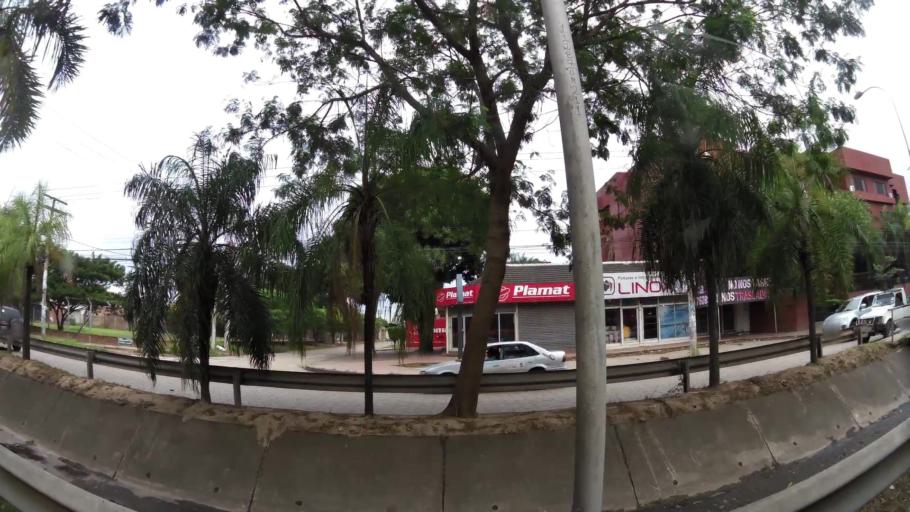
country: BO
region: Santa Cruz
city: Santa Cruz de la Sierra
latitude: -17.7612
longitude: -63.1754
